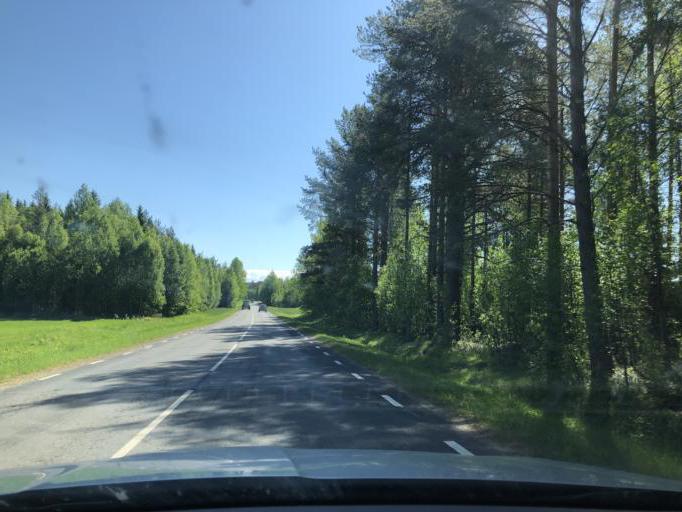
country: SE
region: Norrbotten
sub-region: Lulea Kommun
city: Gammelstad
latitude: 65.6610
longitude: 21.9808
